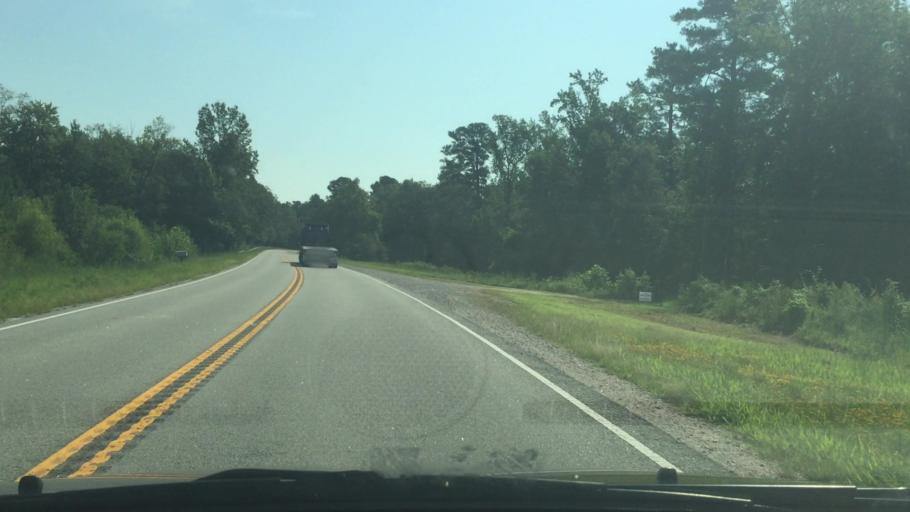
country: US
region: Virginia
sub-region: Sussex County
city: Sussex
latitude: 36.9769
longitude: -77.2195
